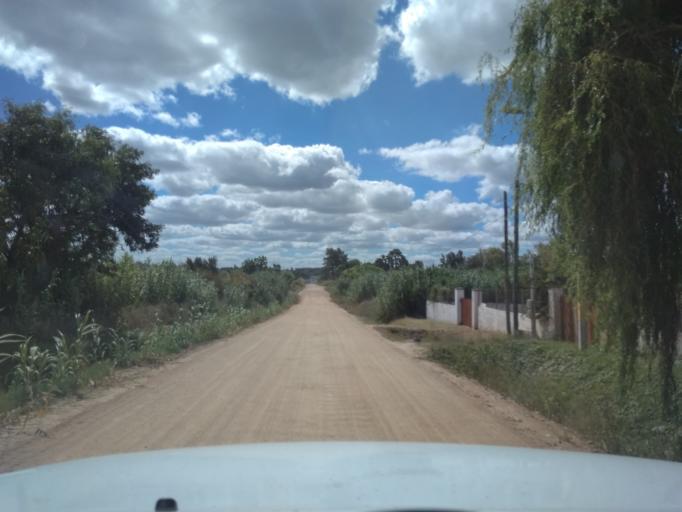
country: UY
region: Canelones
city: Colonia Nicolich
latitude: -34.8280
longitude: -55.9933
